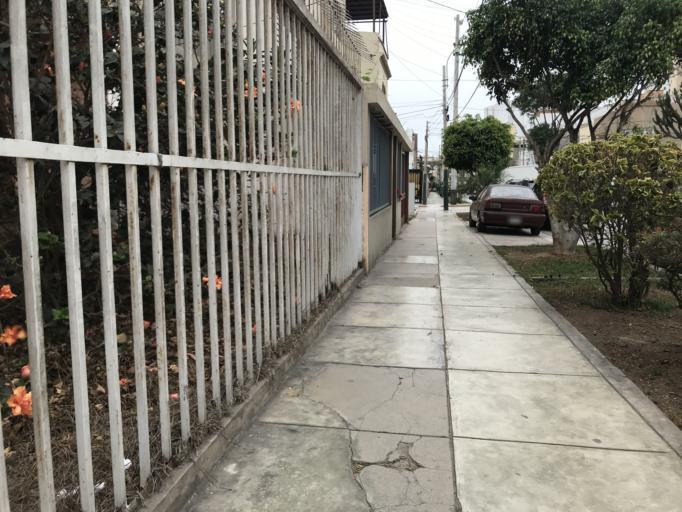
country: PE
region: Lima
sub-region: Lima
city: San Isidro
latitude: -12.0915
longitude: -77.0663
